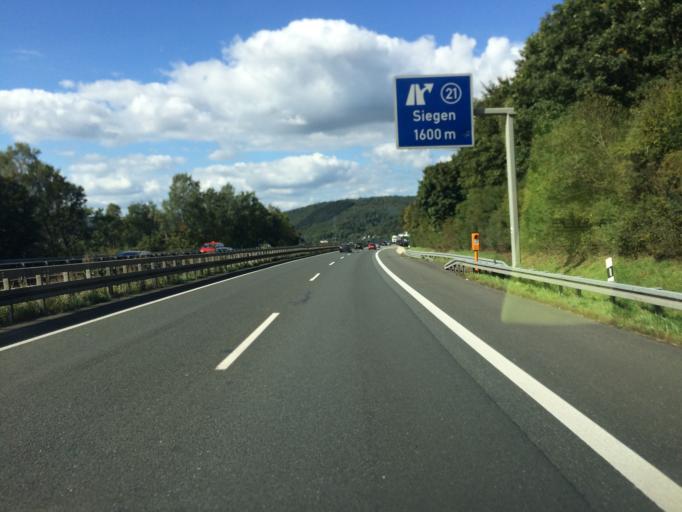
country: DE
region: North Rhine-Westphalia
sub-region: Regierungsbezirk Arnsberg
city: Siegen
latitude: 50.8429
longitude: 7.9961
